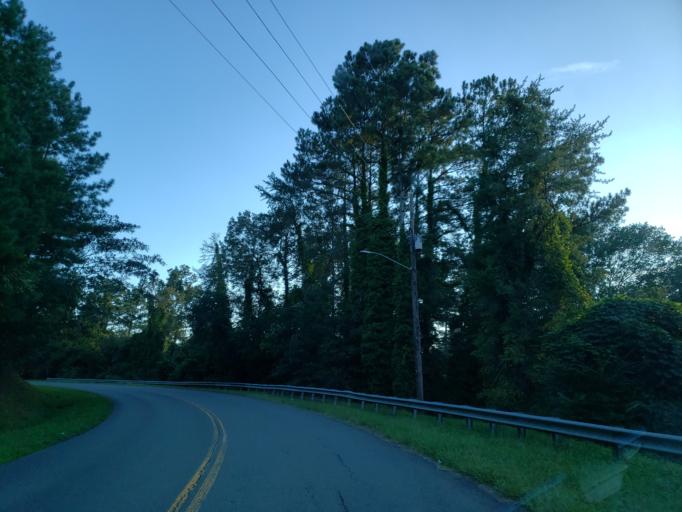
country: US
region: Georgia
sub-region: Floyd County
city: Rome
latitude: 34.2538
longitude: -85.1381
